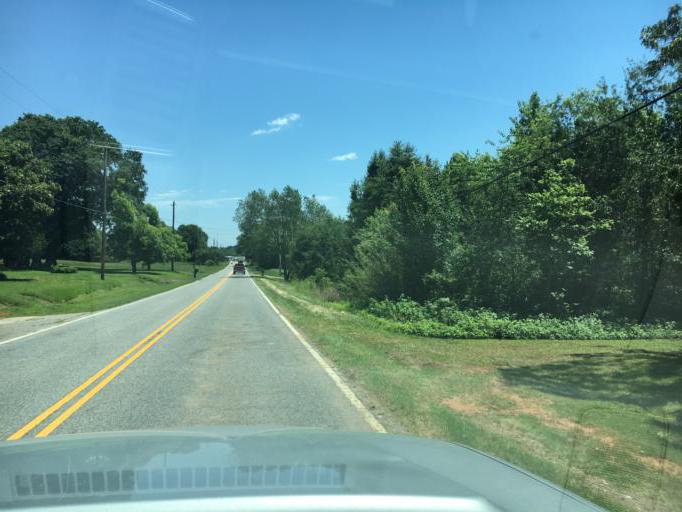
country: US
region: South Carolina
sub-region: Spartanburg County
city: Duncan
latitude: 34.9596
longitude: -82.1808
